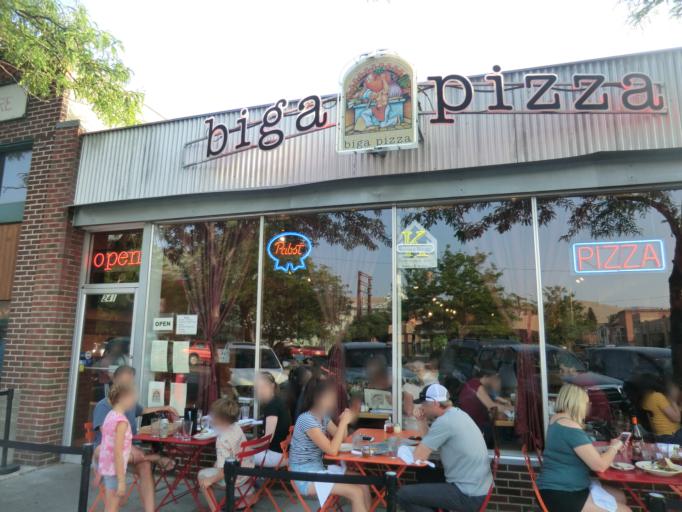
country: US
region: Montana
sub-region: Missoula County
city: Missoula
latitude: 46.8719
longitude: -113.9974
